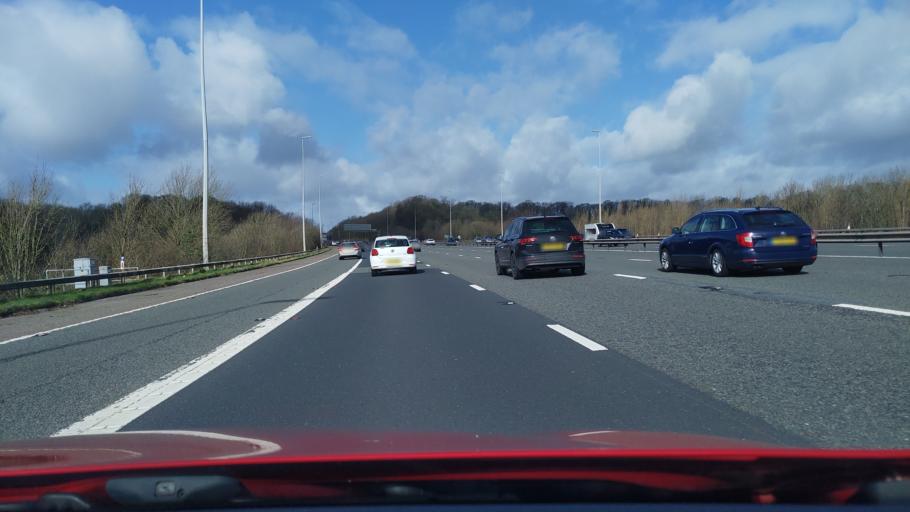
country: GB
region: England
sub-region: Lancashire
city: Goosnargh
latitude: 53.7714
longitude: -2.6389
